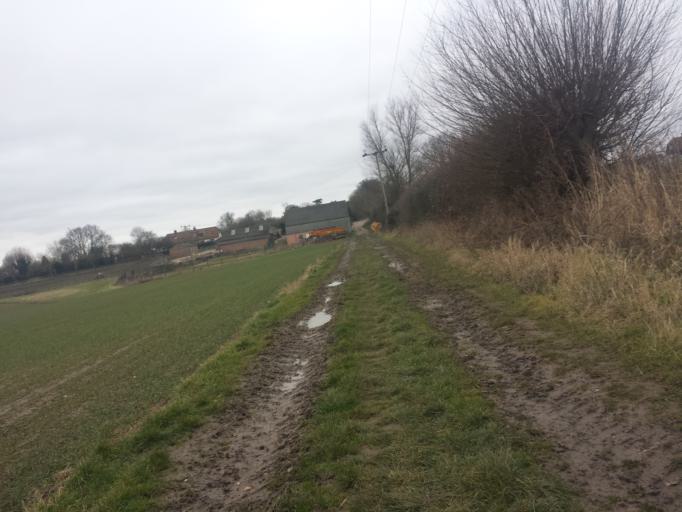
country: GB
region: England
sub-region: Essex
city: Little Clacton
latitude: 51.8813
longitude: 1.1695
